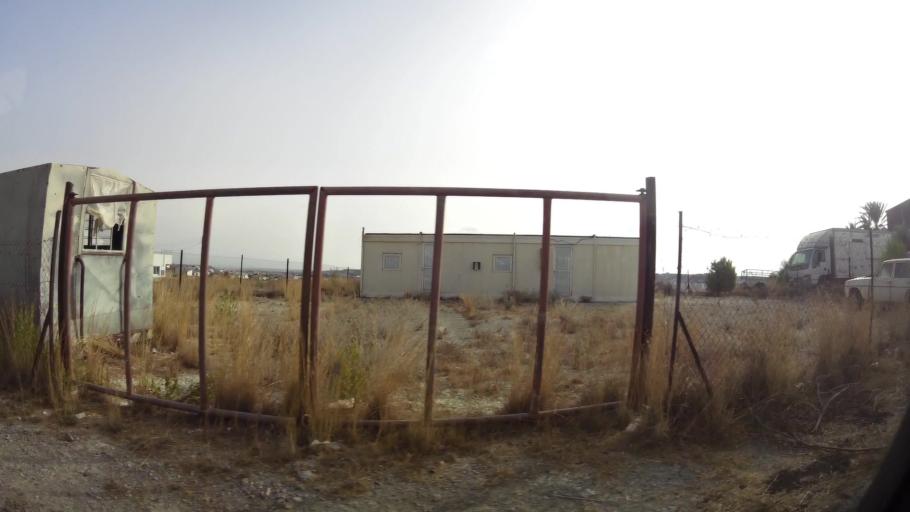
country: CY
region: Lefkosia
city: Geri
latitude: 35.0712
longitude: 33.3902
